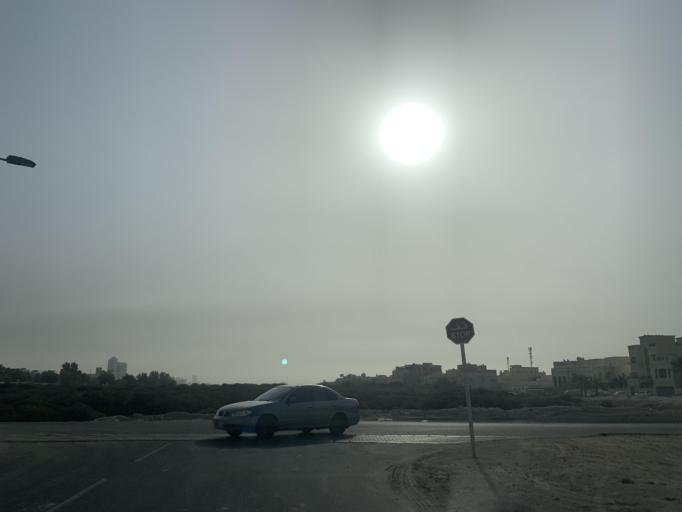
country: BH
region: Northern
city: Madinat `Isa
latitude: 26.1957
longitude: 50.5593
